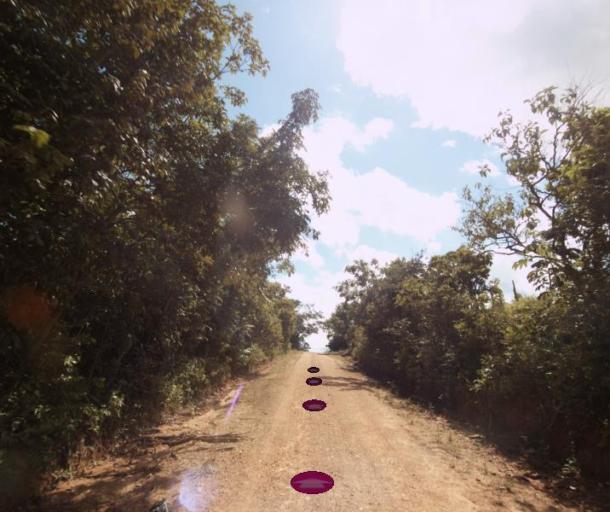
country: BR
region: Goias
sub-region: Pirenopolis
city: Pirenopolis
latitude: -15.7788
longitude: -48.9718
